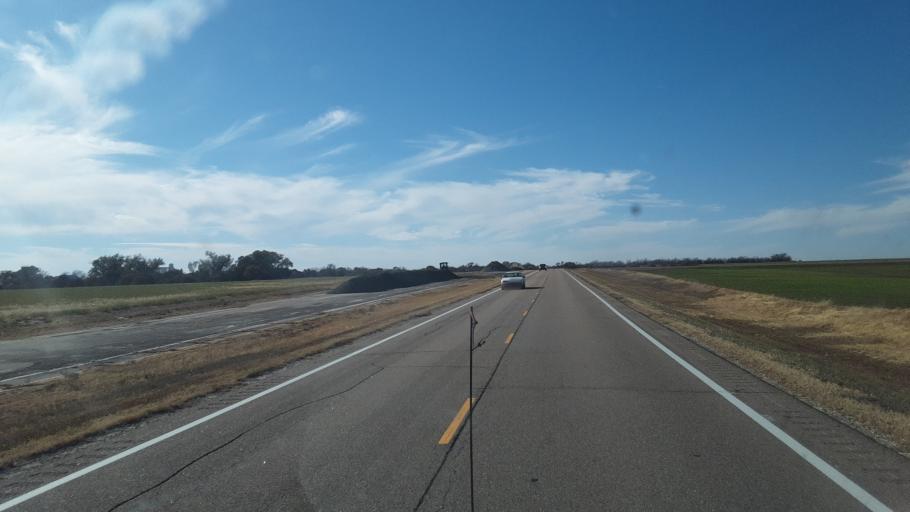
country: US
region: Kansas
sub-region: Pawnee County
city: Larned
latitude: 38.1894
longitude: -99.2910
